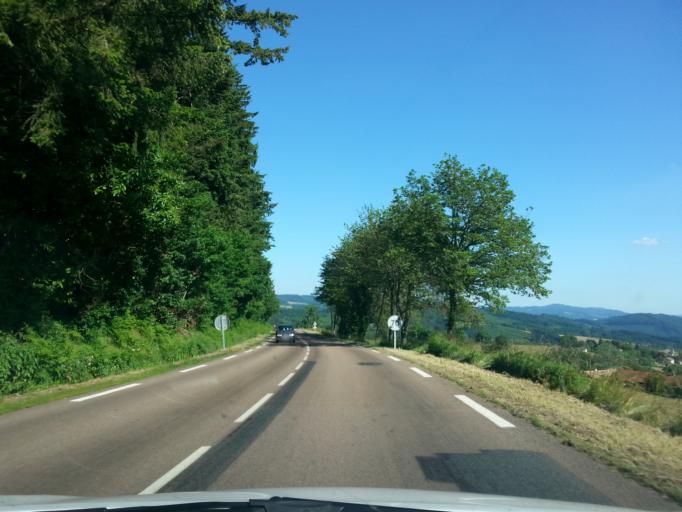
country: FR
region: Rhone-Alpes
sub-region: Departement de la Loire
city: Belmont-de-la-Loire
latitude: 46.1619
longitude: 4.4508
